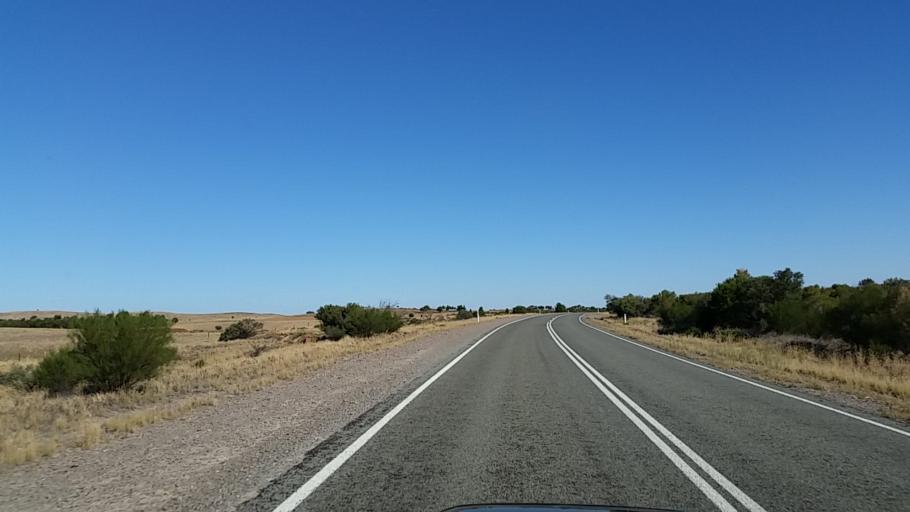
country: AU
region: South Australia
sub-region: Peterborough
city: Peterborough
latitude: -32.5437
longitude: 138.5599
